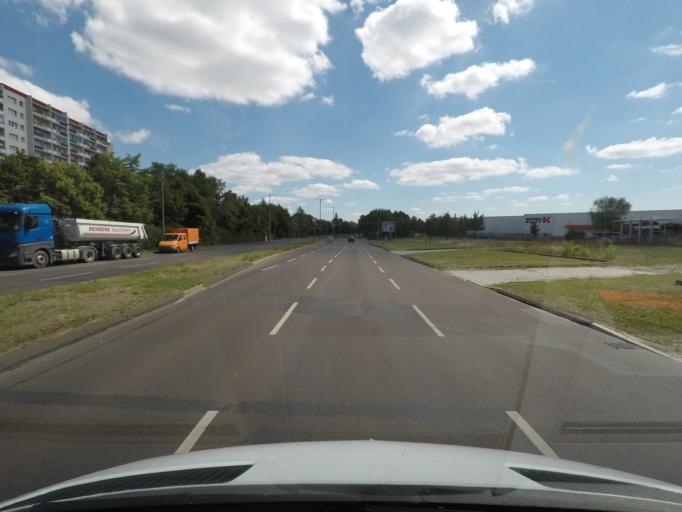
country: DE
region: Berlin
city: Biesdorf
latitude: 52.5216
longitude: 13.5411
